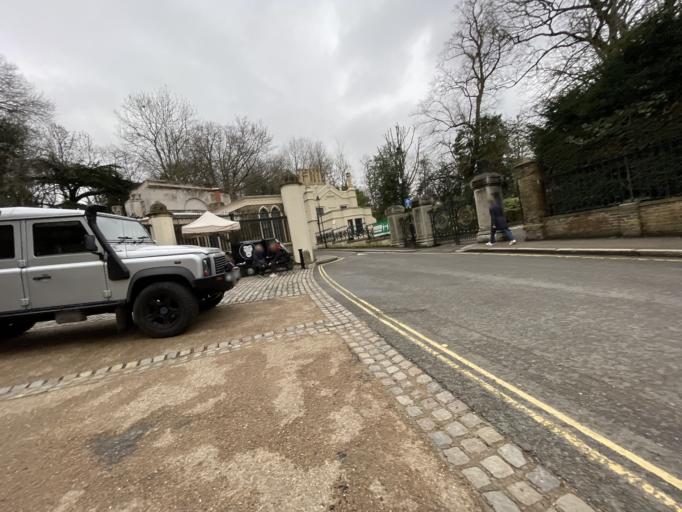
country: GB
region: England
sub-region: Greater London
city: Holloway
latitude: 51.5670
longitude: -0.1466
